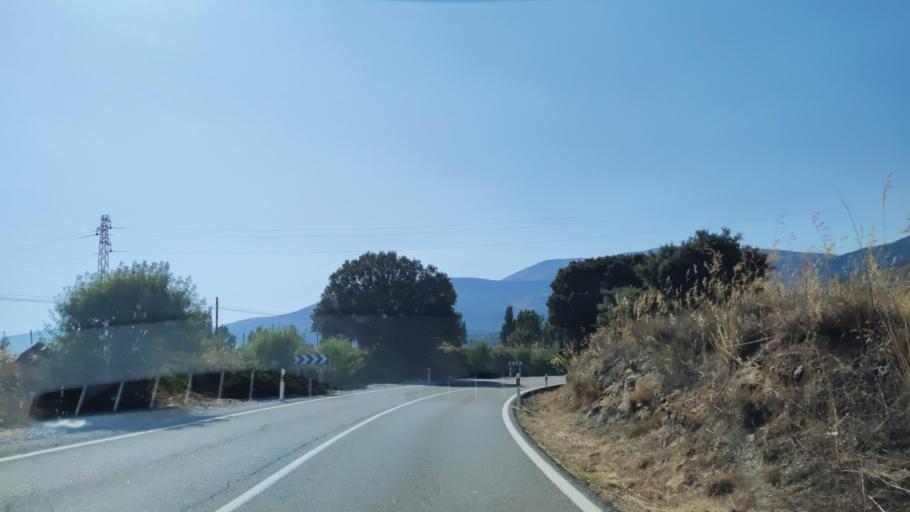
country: ES
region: Madrid
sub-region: Provincia de Madrid
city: Lozoya
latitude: 40.9490
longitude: -3.7750
